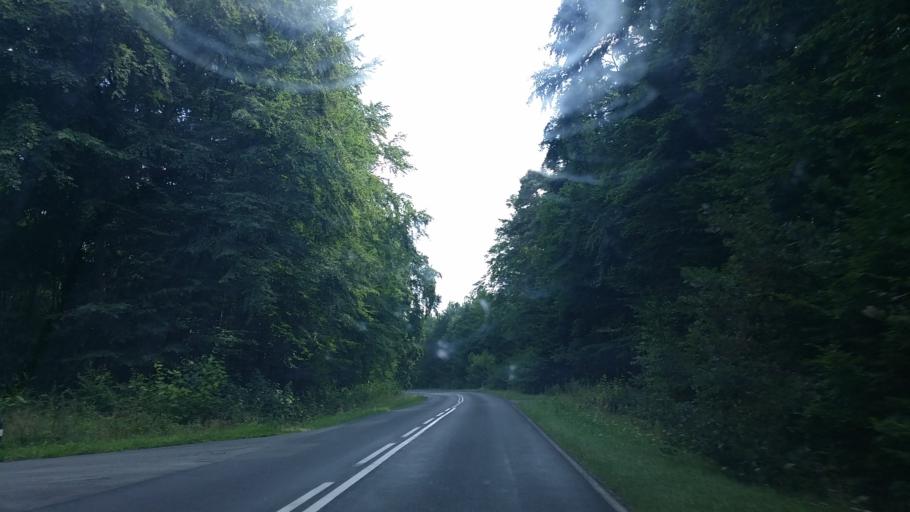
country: PL
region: Lubusz
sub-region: Powiat gorzowski
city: Klodawa
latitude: 52.8567
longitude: 15.2002
